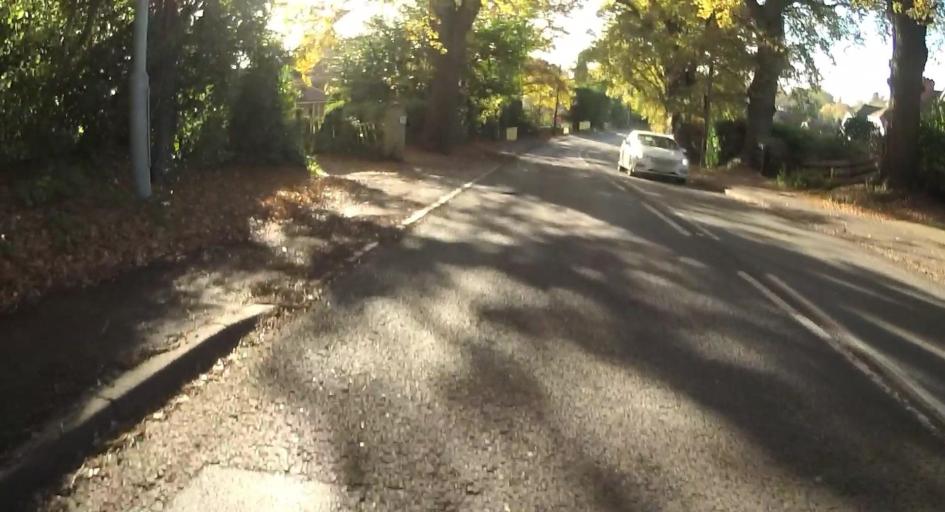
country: GB
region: England
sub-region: Wokingham
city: Barkham
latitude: 51.3998
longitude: -0.8684
